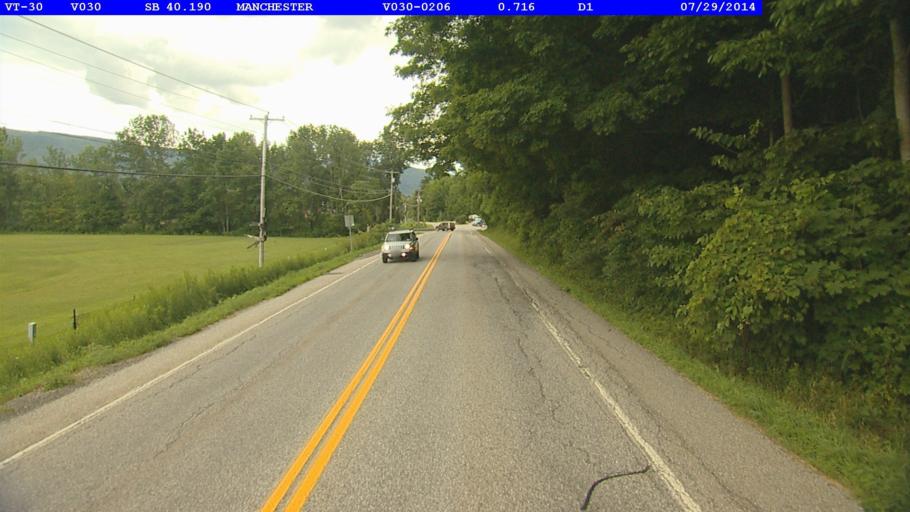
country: US
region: Vermont
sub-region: Bennington County
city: Manchester Center
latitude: 43.1871
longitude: -73.0576
